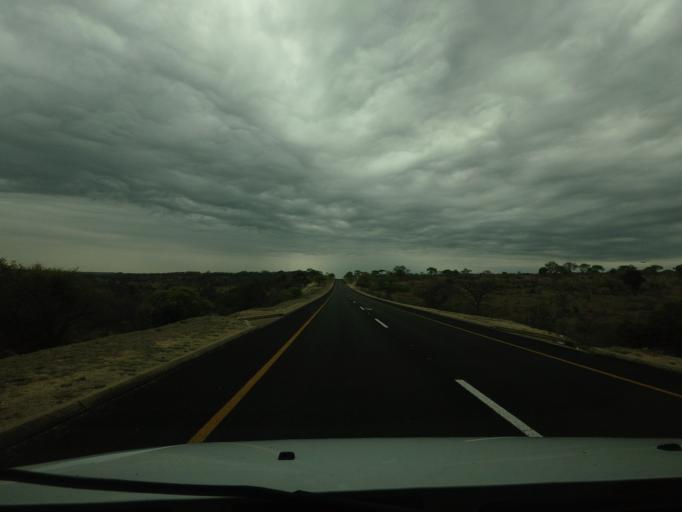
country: ZA
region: Limpopo
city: Thulamahashi
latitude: -24.5687
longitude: 31.0730
